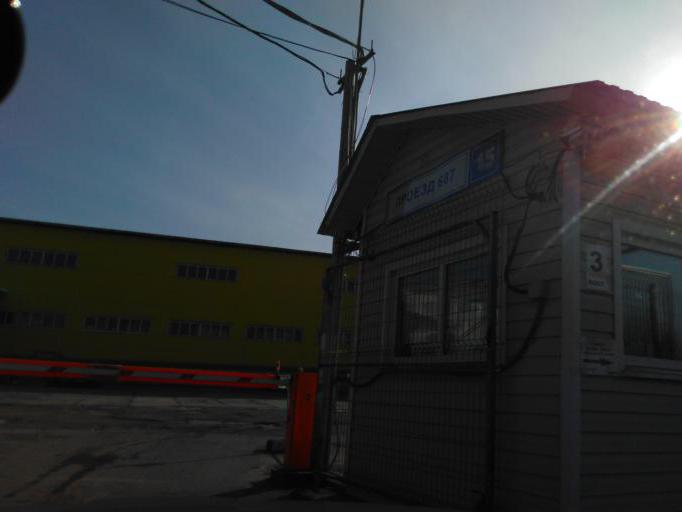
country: RU
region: Moscow
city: Zelenograd
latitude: 55.9644
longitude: 37.1631
